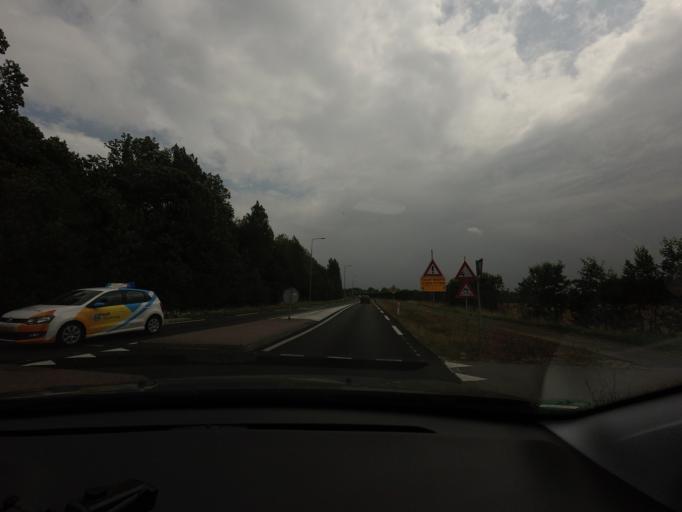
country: NL
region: Gelderland
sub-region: Gemeente Tiel
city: Tiel
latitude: 51.8880
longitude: 5.3898
